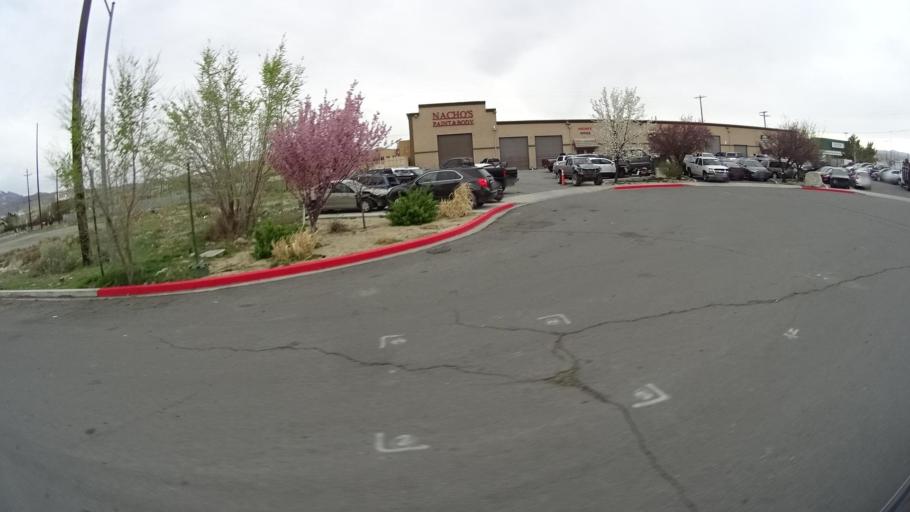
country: US
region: Nevada
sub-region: Washoe County
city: Reno
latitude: 39.5283
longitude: -119.7910
